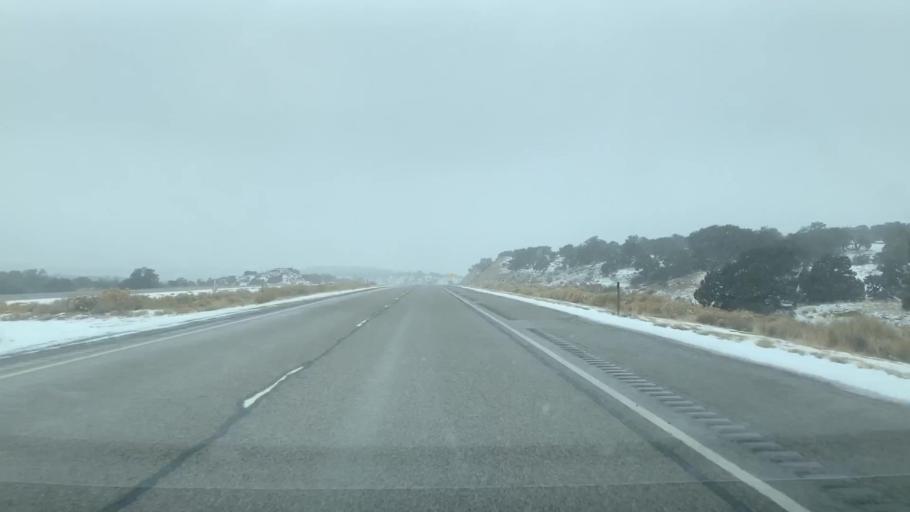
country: US
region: Utah
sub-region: Emery County
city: Ferron
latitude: 38.8593
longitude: -110.8286
